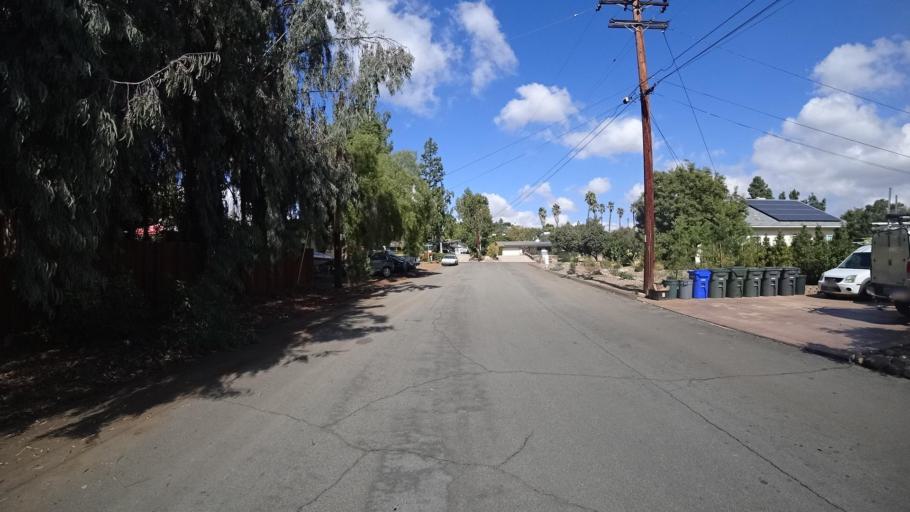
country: US
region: California
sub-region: San Diego County
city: Rancho San Diego
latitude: 32.7595
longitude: -116.9467
